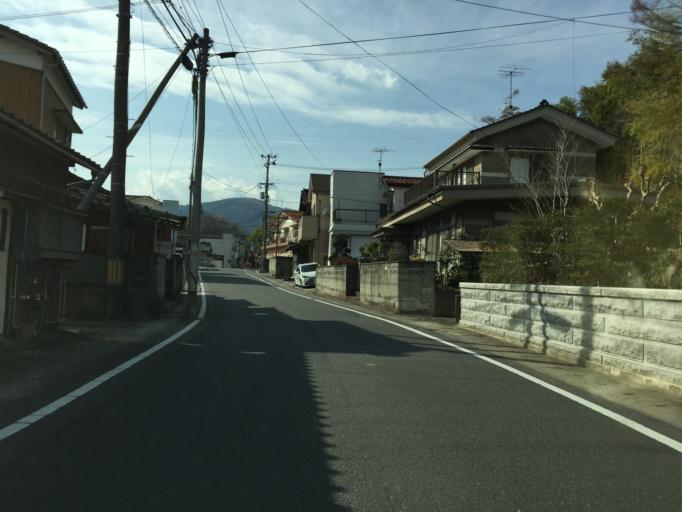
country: JP
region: Fukushima
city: Iwaki
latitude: 37.0058
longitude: 140.8395
